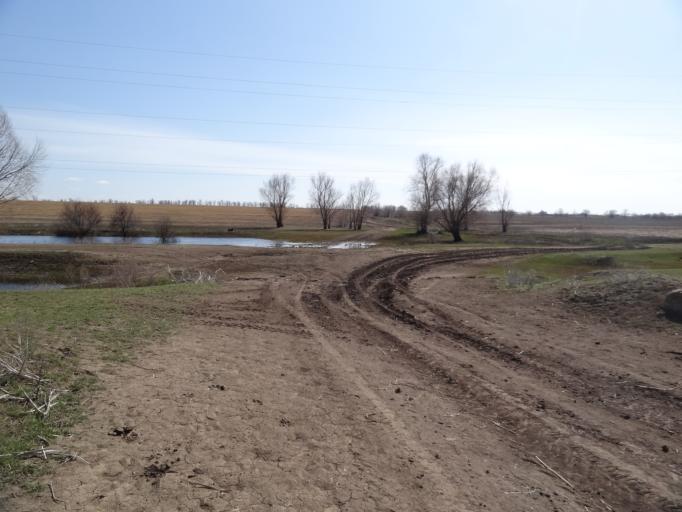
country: RU
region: Saratov
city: Engel's
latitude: 51.4026
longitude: 46.2232
